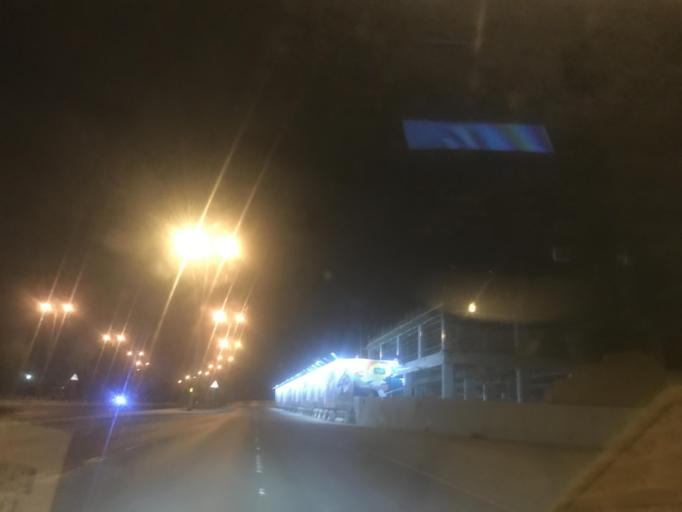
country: SA
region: Ar Riyad
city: Riyadh
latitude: 24.7855
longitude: 46.5911
